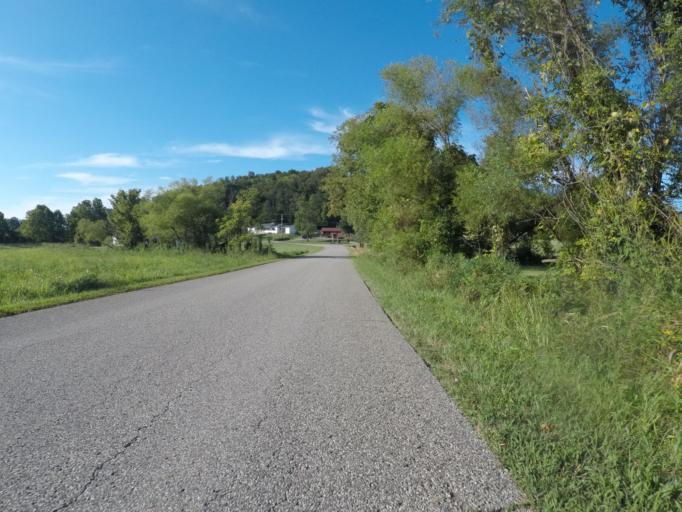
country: US
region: West Virginia
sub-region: Cabell County
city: Huntington
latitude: 38.5019
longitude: -82.4879
